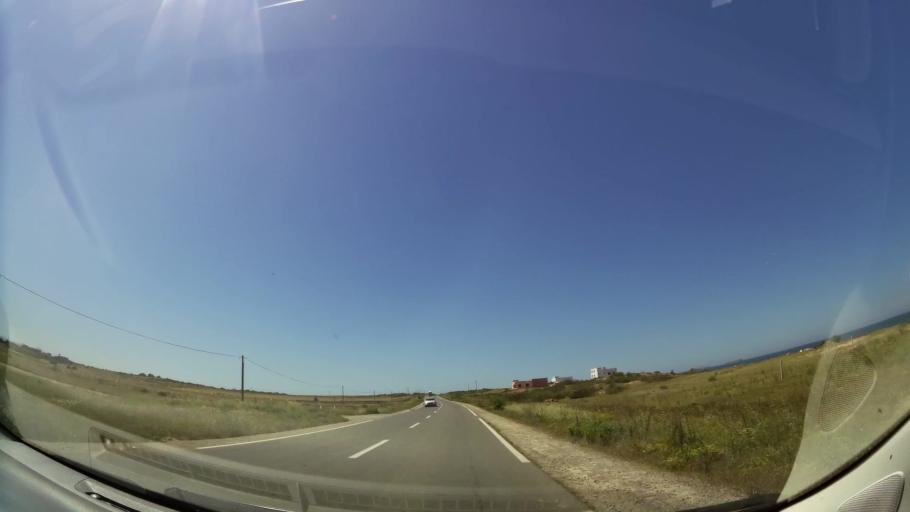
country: MA
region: Oriental
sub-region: Berkane-Taourirt
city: Madagh
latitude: 35.1258
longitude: -2.3873
